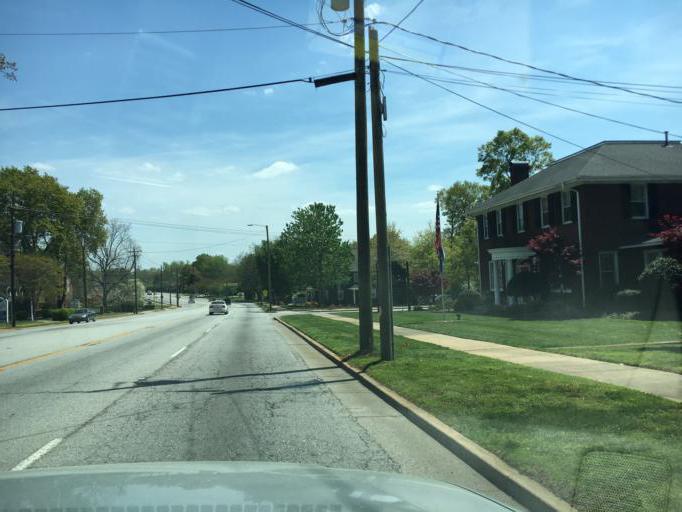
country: US
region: South Carolina
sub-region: Spartanburg County
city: Spartanburg
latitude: 34.9463
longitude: -81.9147
